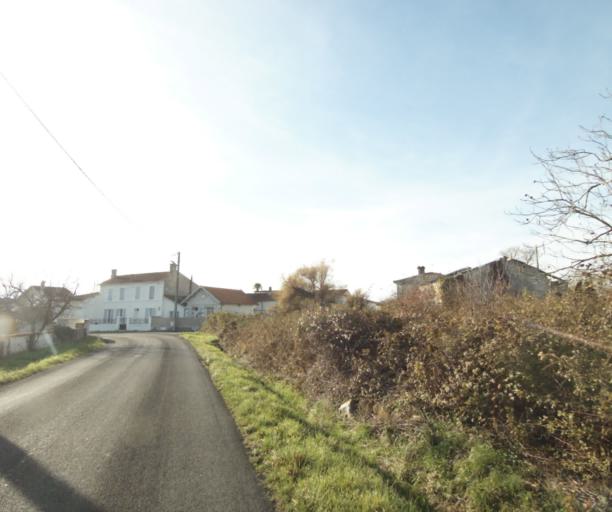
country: FR
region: Poitou-Charentes
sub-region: Departement de la Charente-Maritime
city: Chaniers
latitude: 45.7108
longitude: -0.5271
